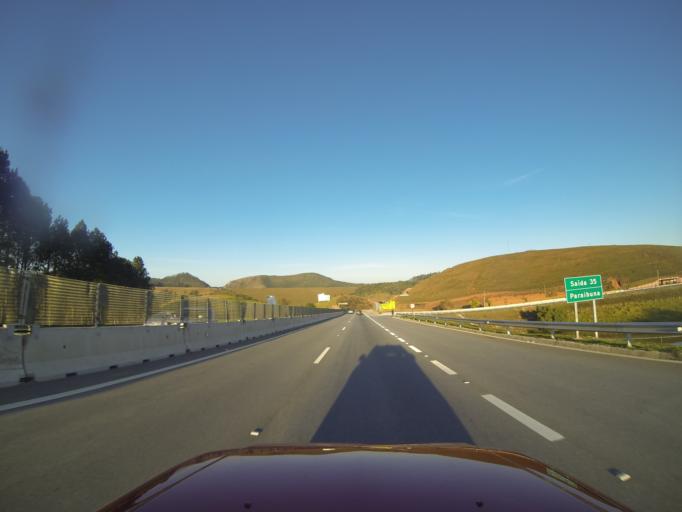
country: BR
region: Sao Paulo
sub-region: Santa Branca
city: Santa Branca
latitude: -23.3707
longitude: -45.6720
